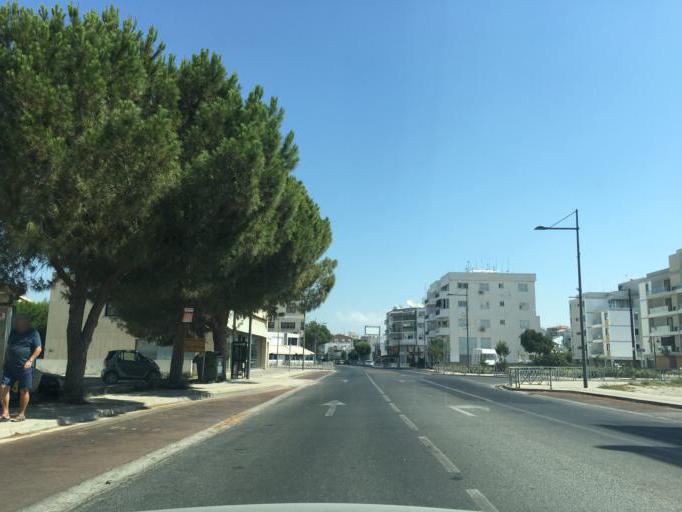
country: CY
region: Lefkosia
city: Nicosia
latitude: 35.1580
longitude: 33.3156
